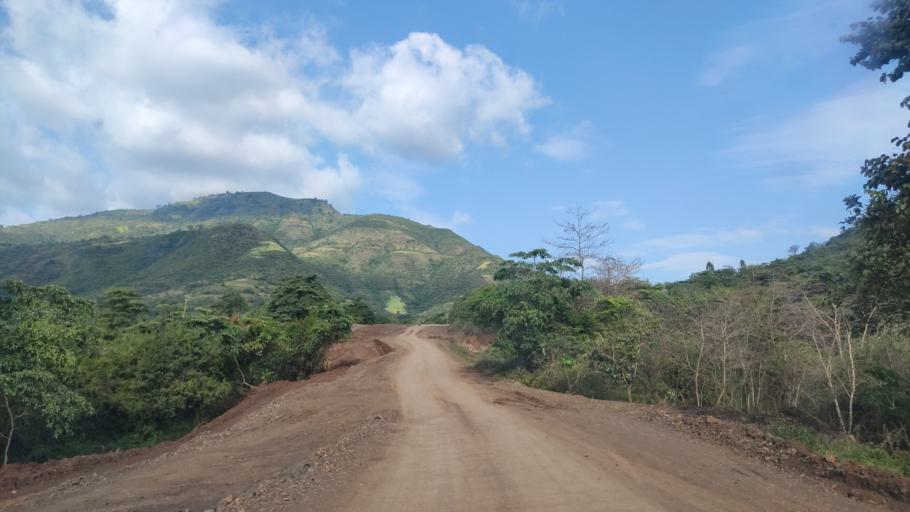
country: ET
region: Southern Nations, Nationalities, and People's Region
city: Arba Minch'
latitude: 6.4251
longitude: 37.3371
